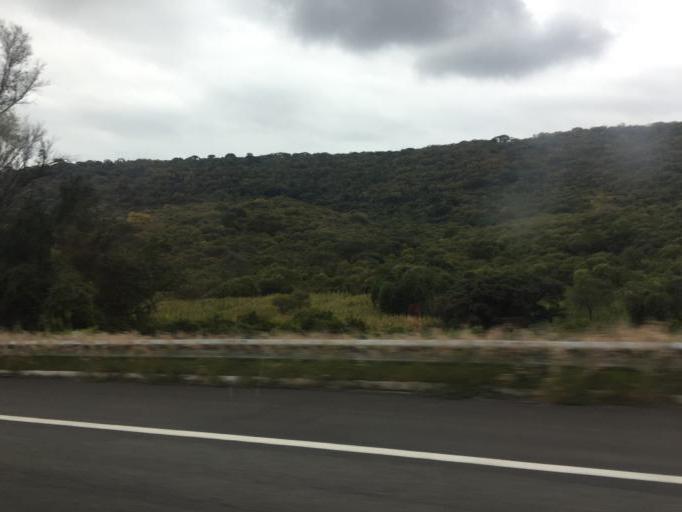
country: MX
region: Jalisco
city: Ocotlan
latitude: 20.4208
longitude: -102.7637
